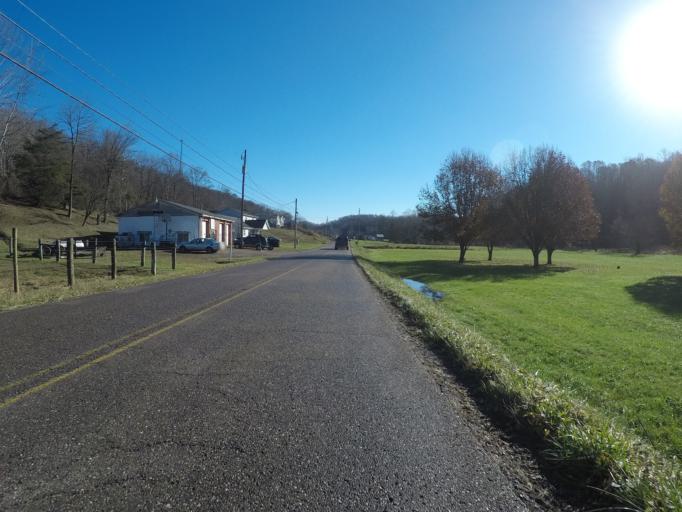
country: US
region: West Virginia
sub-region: Cabell County
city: Huntington
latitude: 38.4820
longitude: -82.4776
